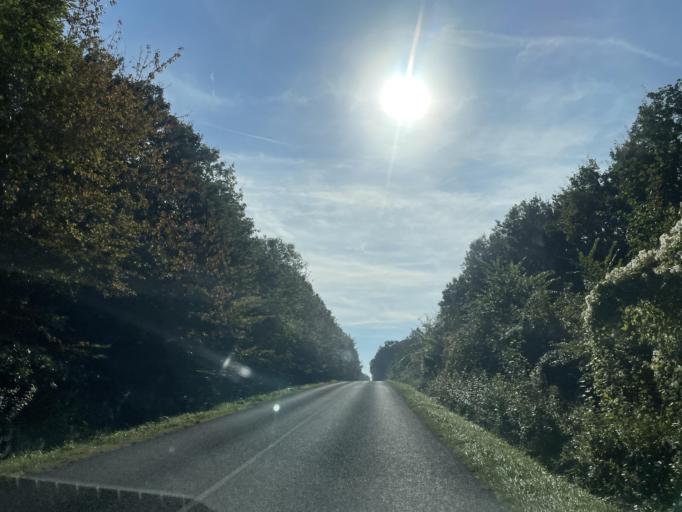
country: FR
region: Ile-de-France
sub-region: Departement de Seine-et-Marne
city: Saint-Jean-les-Deux-Jumeaux
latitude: 48.9551
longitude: 2.9862
